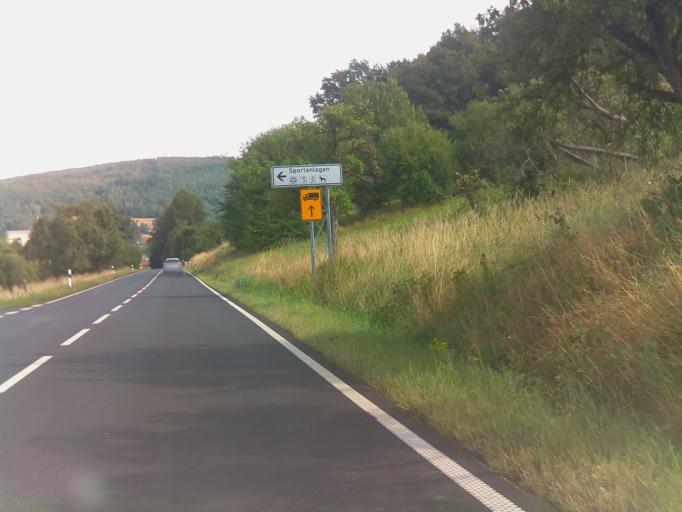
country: DE
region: Hesse
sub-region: Regierungsbezirk Darmstadt
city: Bad Orb
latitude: 50.2324
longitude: 9.3333
